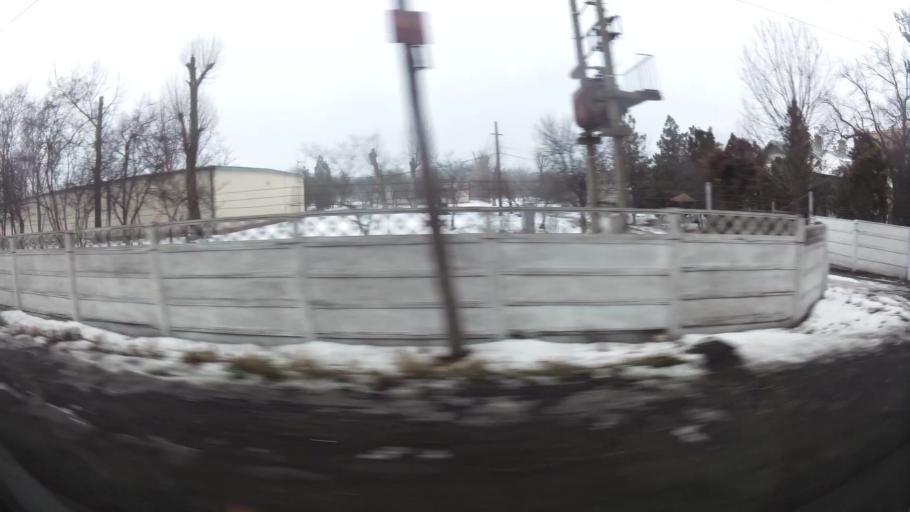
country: RO
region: Ilfov
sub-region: Comuna Clinceni
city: Olteni
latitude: 44.4189
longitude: 25.9695
